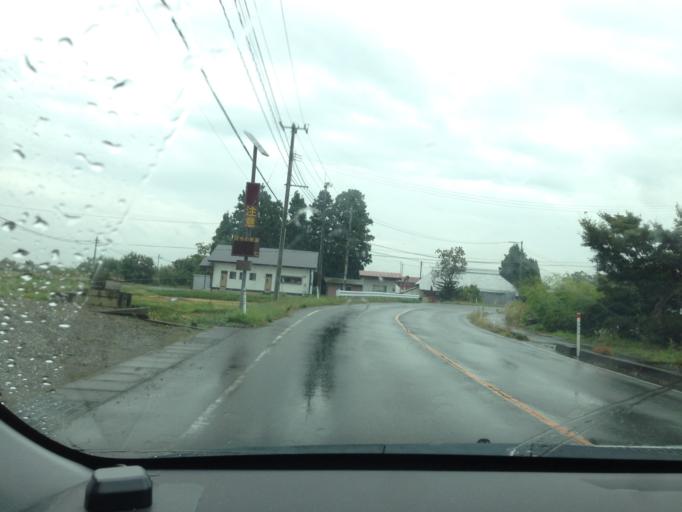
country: JP
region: Fukushima
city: Kitakata
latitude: 37.5098
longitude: 139.8344
